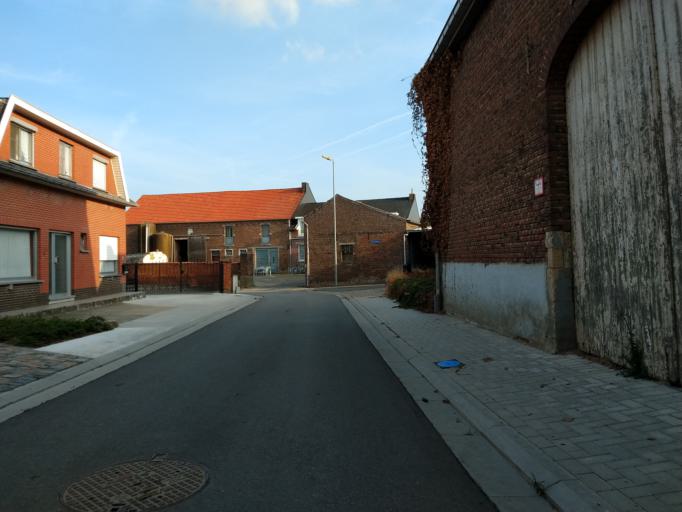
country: BE
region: Flanders
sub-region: Provincie Vlaams-Brabant
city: Boutersem
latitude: 50.8106
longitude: 4.8403
